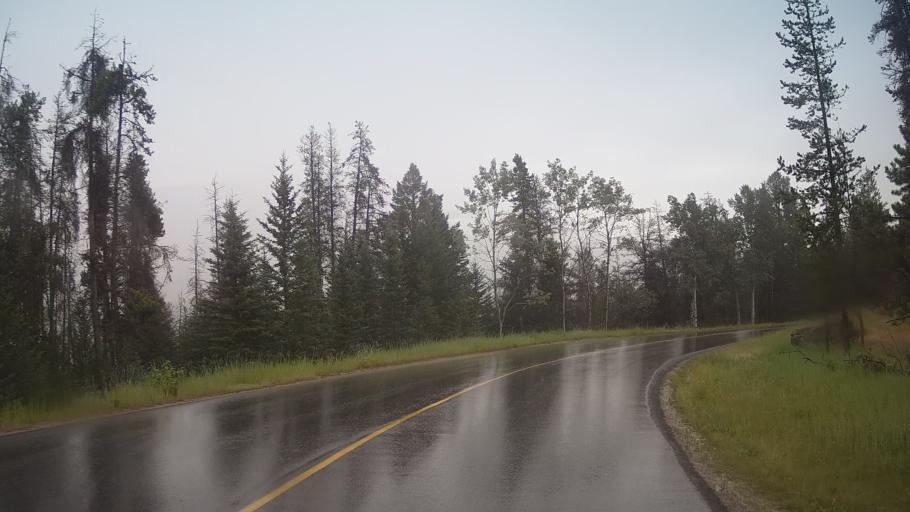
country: CA
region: Alberta
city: Jasper Park Lodge
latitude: 52.8910
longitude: -118.0817
